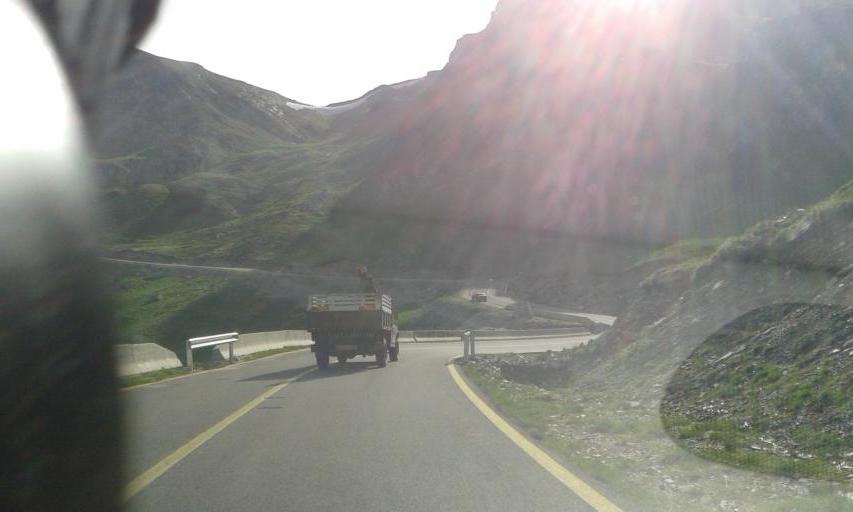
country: RO
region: Gorj
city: Novaci-Straini
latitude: 45.3581
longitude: 23.6547
